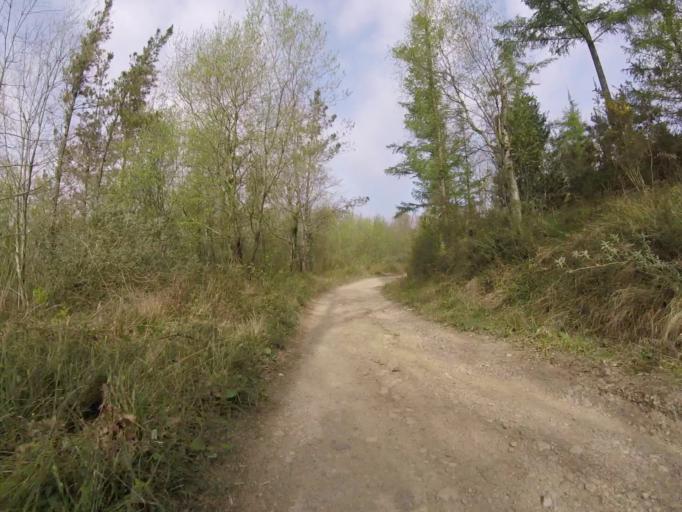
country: ES
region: Basque Country
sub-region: Provincia de Guipuzcoa
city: Usurbil
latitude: 43.2448
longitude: -2.0830
